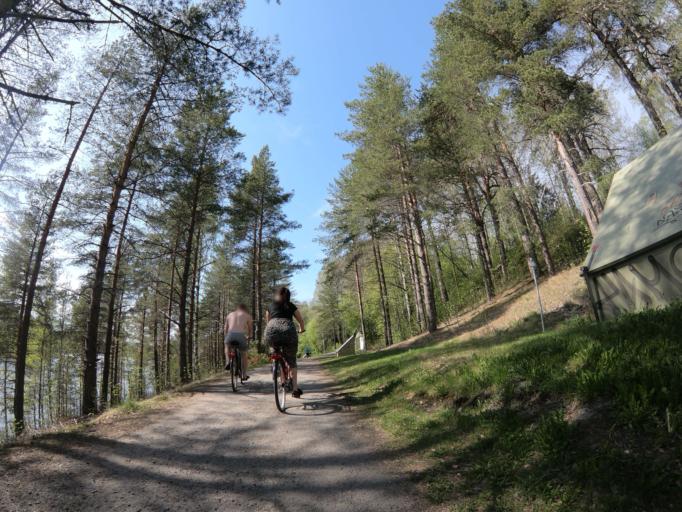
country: SE
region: Vaesterbotten
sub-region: Umea Kommun
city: Roback
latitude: 63.8299
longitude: 20.1634
